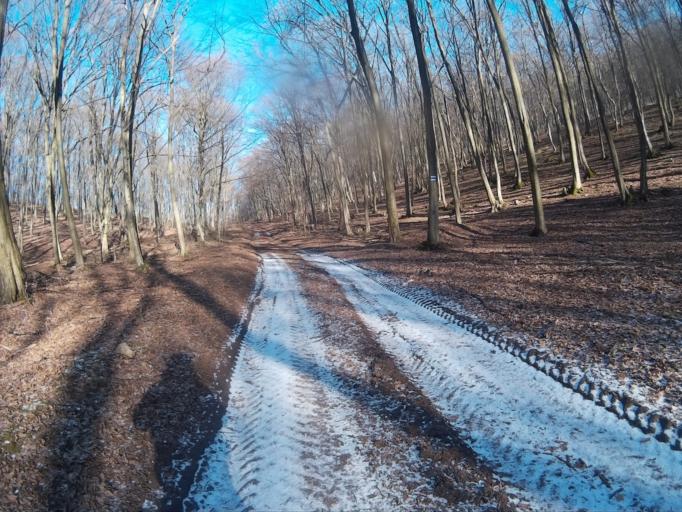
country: HU
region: Borsod-Abauj-Zemplen
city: Rudabanya
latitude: 48.5061
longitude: 20.6051
